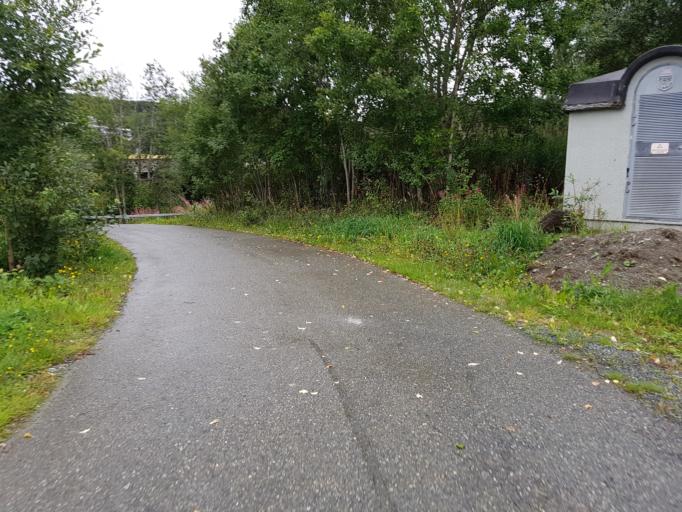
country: NO
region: Sor-Trondelag
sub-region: Trondheim
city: Trondheim
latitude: 63.4106
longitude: 10.4755
